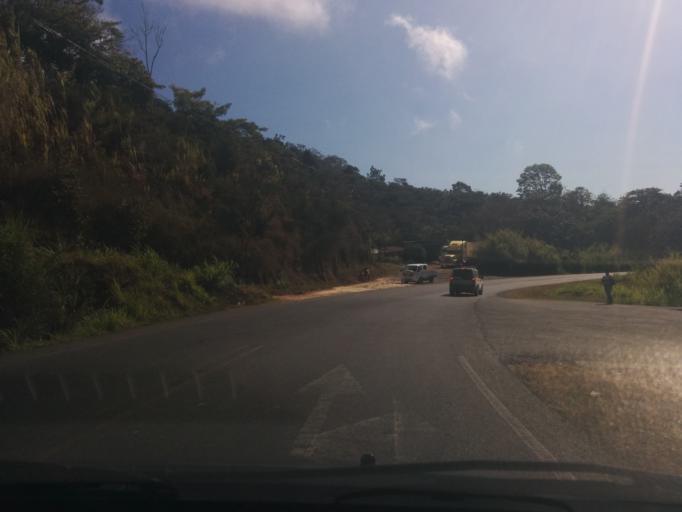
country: CR
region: Alajuela
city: San Rafael
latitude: 10.0700
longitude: -84.4933
